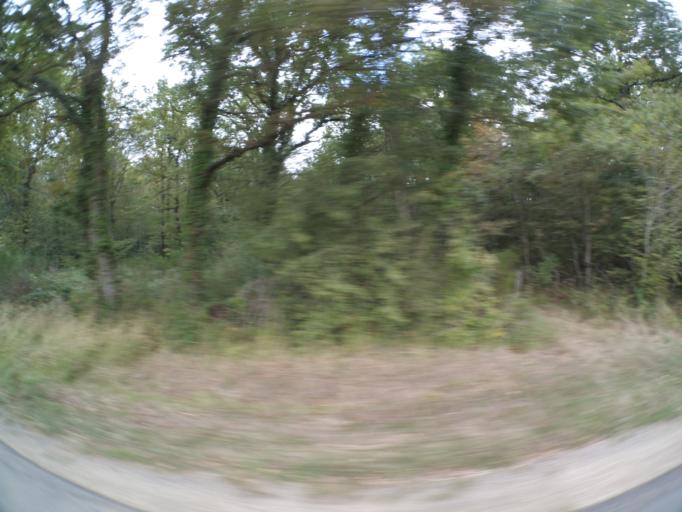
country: FR
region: Centre
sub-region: Departement d'Indre-et-Loire
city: Auzouer-en-Touraine
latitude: 47.5143
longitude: 0.9594
